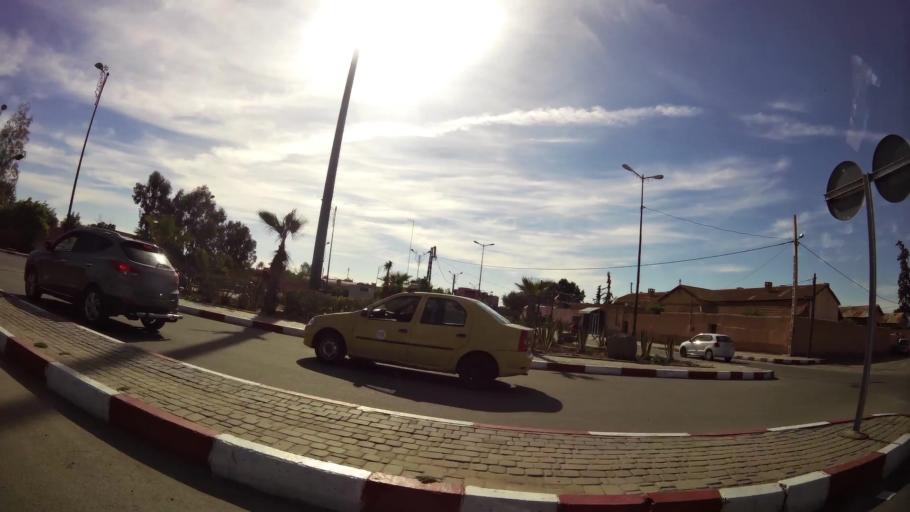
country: MA
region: Marrakech-Tensift-Al Haouz
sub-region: Marrakech
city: Marrakesh
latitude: 31.6432
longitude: -8.0366
